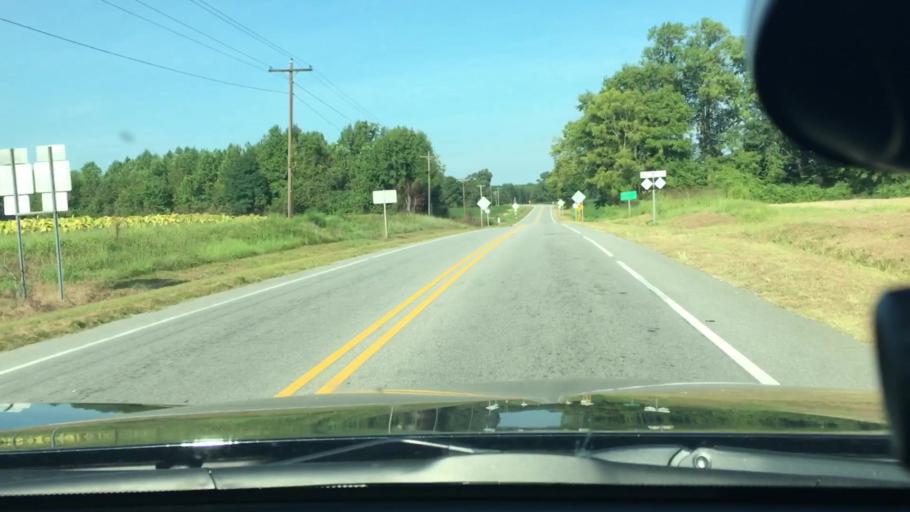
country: US
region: North Carolina
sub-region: Edgecombe County
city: Pinetops
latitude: 35.7813
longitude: -77.6052
